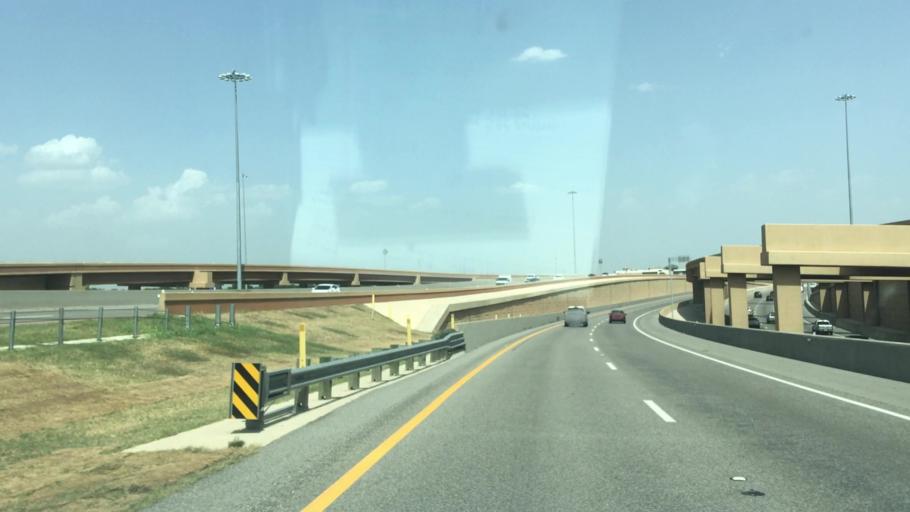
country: US
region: Texas
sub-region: Tarrant County
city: Bedford
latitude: 32.8400
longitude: -97.1551
